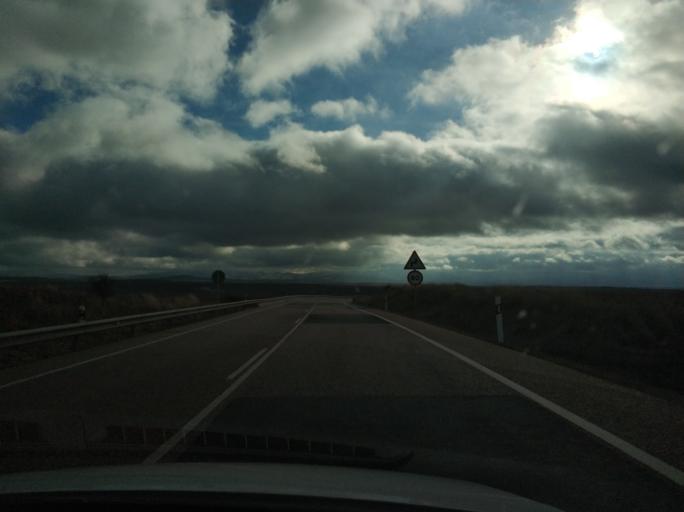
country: ES
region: Castille and Leon
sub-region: Provincia de Segovia
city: Ayllon
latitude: 41.4466
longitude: -3.3413
